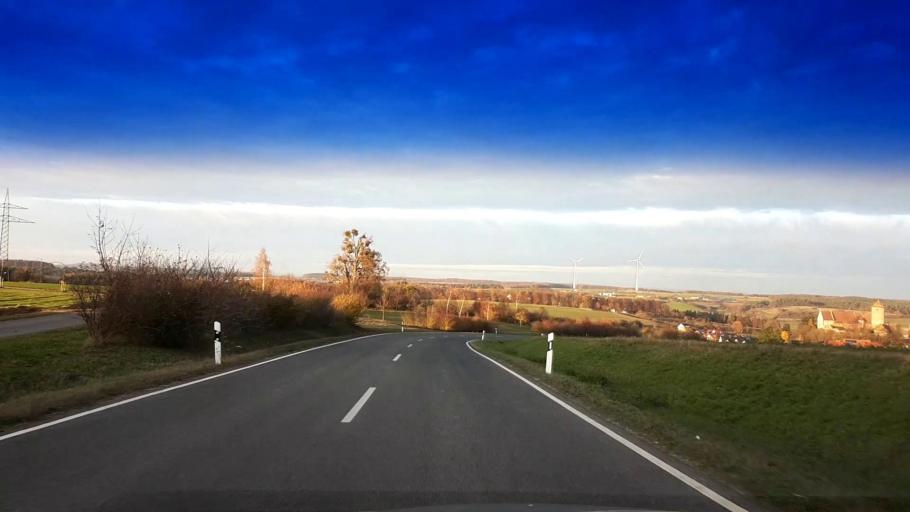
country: DE
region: Bavaria
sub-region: Upper Franconia
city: Priesendorf
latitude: 49.8787
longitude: 10.7221
